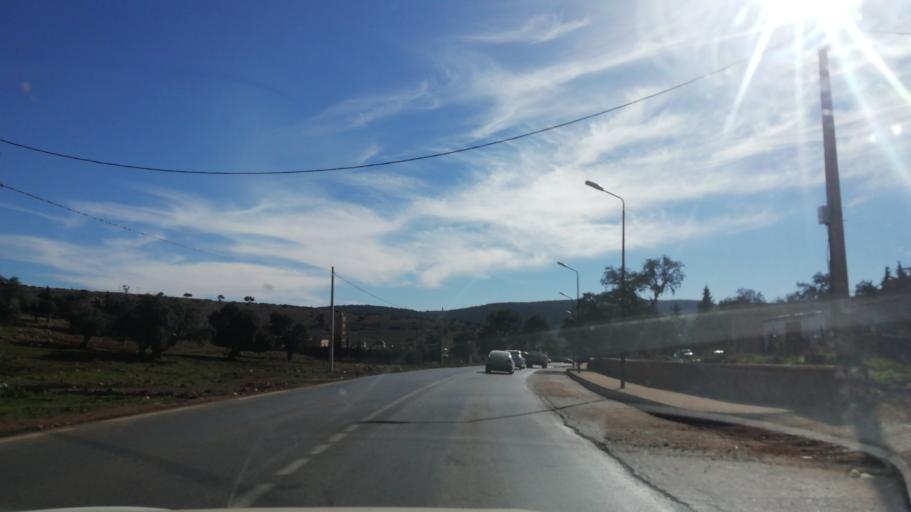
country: DZ
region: Tlemcen
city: Sebdou
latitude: 34.7278
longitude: -1.3372
